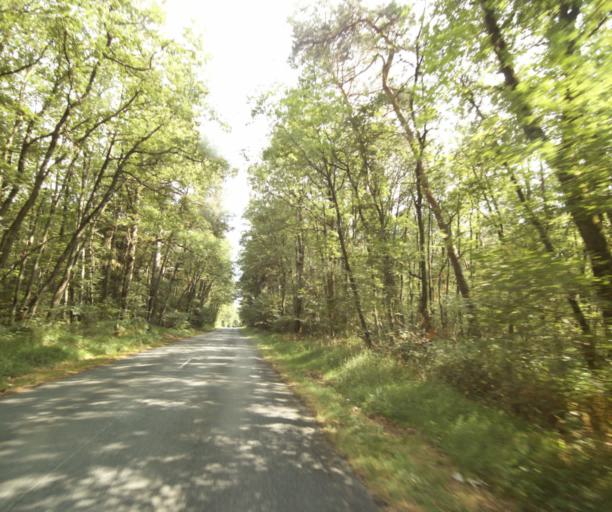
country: FR
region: Ile-de-France
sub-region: Departement de Seine-et-Marne
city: Acheres-la-Foret
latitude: 48.3669
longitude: 2.5641
